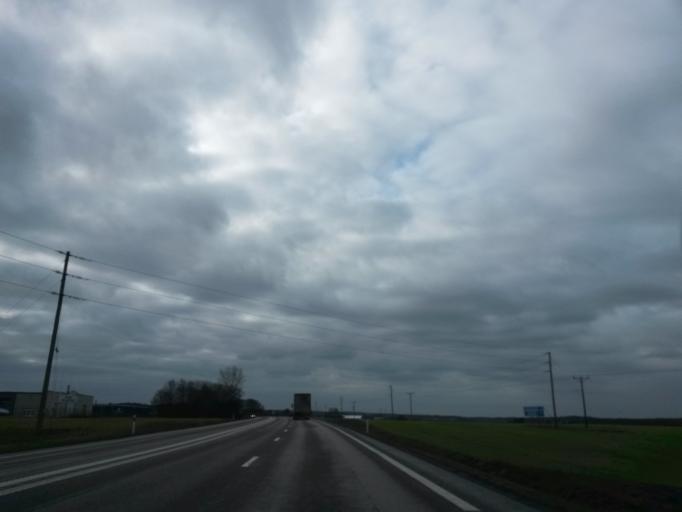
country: SE
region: Vaestra Goetaland
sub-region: Vargarda Kommun
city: Vargarda
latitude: 58.0383
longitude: 12.7915
